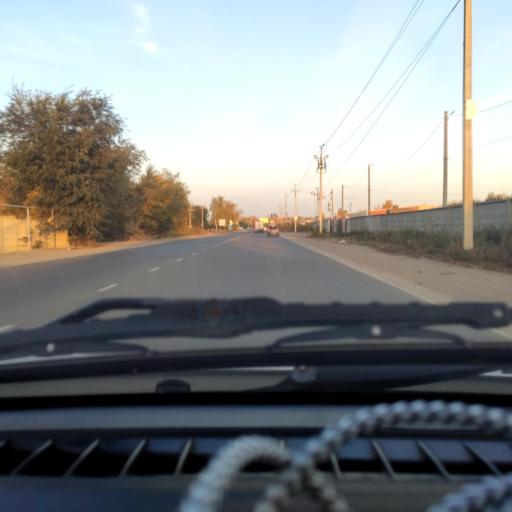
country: RU
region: Samara
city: Tol'yatti
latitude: 53.5282
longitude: 49.4748
